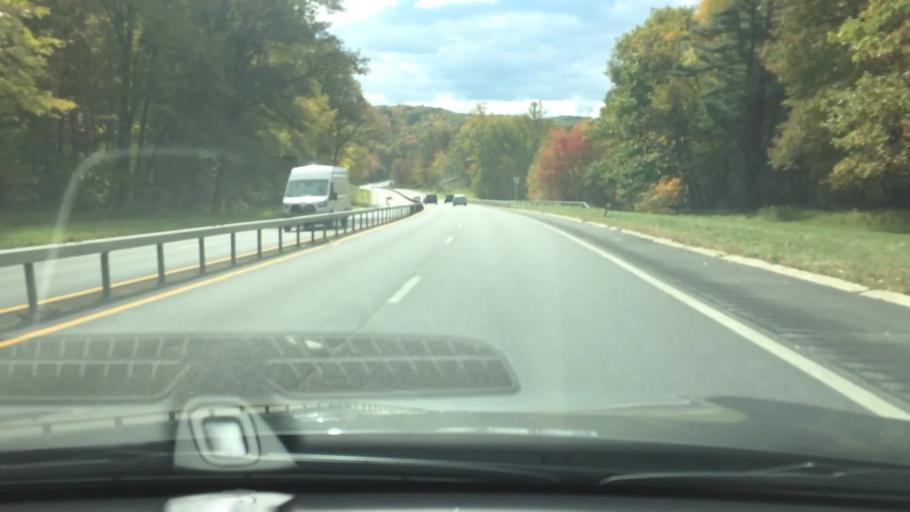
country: US
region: New York
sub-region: Dutchess County
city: Brinckerhoff
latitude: 41.5065
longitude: -73.7950
